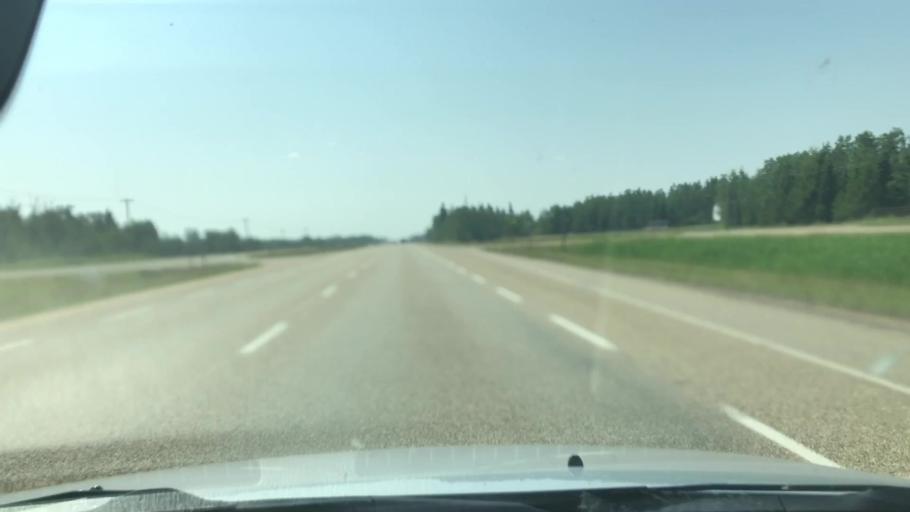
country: CA
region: Alberta
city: Devon
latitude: 53.4368
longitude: -113.7632
